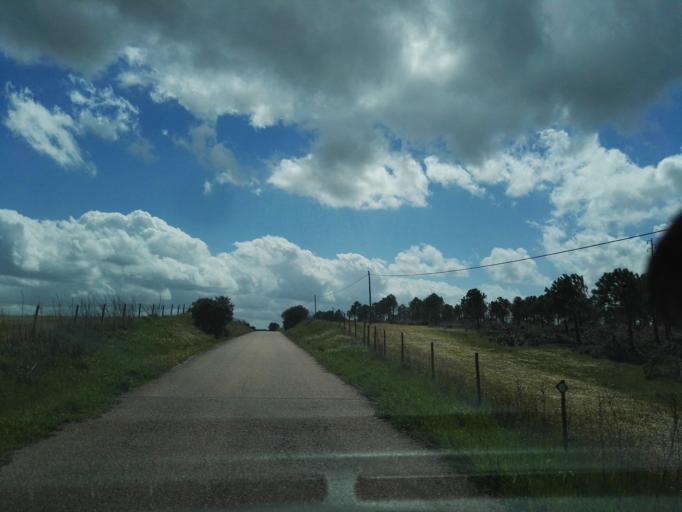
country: PT
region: Portalegre
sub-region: Elvas
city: Elvas
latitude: 38.9748
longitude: -7.1743
